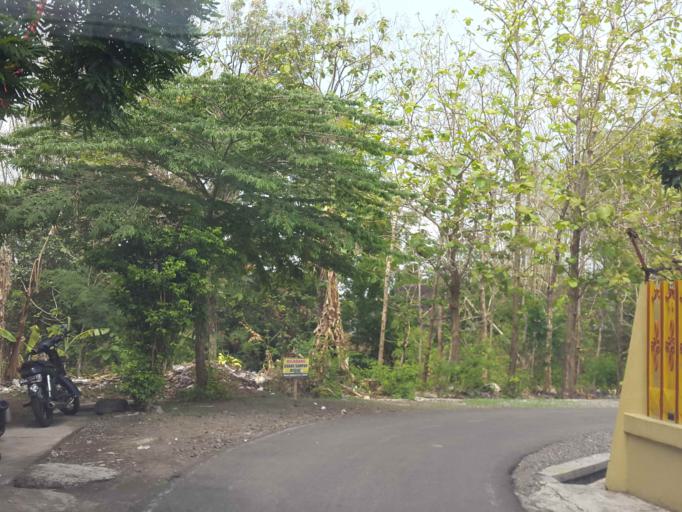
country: ID
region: Central Java
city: Jaten
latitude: -7.5970
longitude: 110.9533
